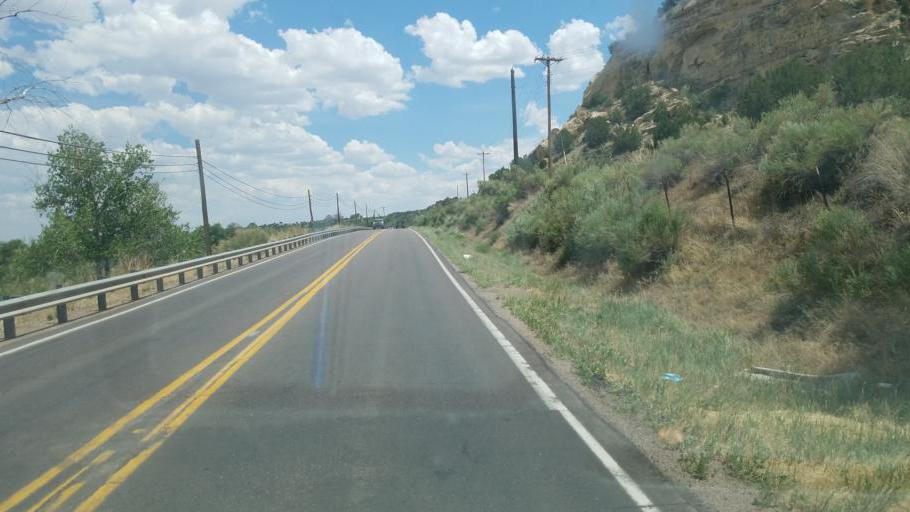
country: US
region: Colorado
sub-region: Fremont County
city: Lincoln Park
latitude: 38.4121
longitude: -105.1754
